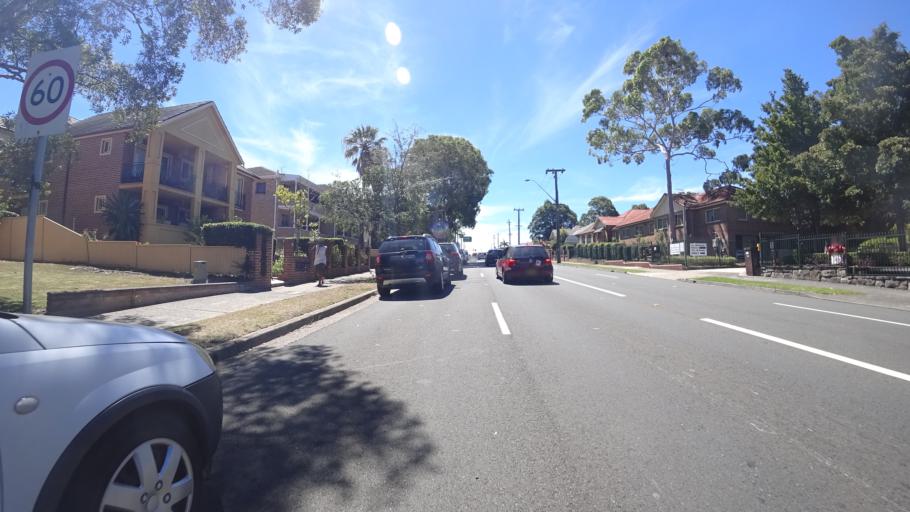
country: AU
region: New South Wales
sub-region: Rockdale
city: Bexley
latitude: -33.9499
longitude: 151.1293
